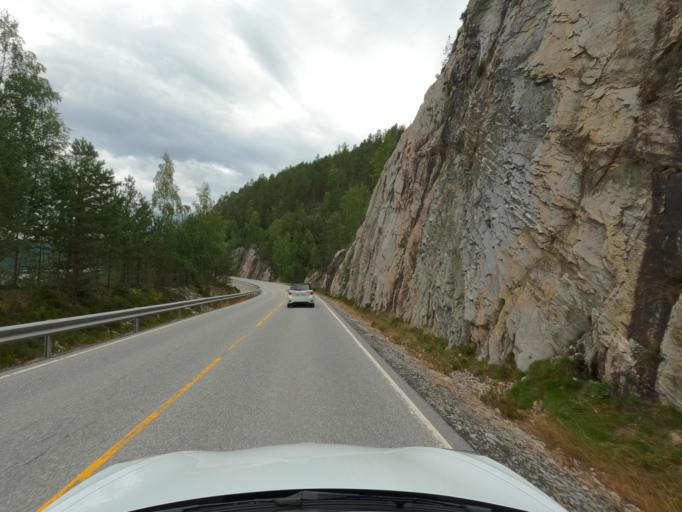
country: NO
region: Telemark
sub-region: Hjartdal
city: Sauland
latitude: 59.7628
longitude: 9.0186
